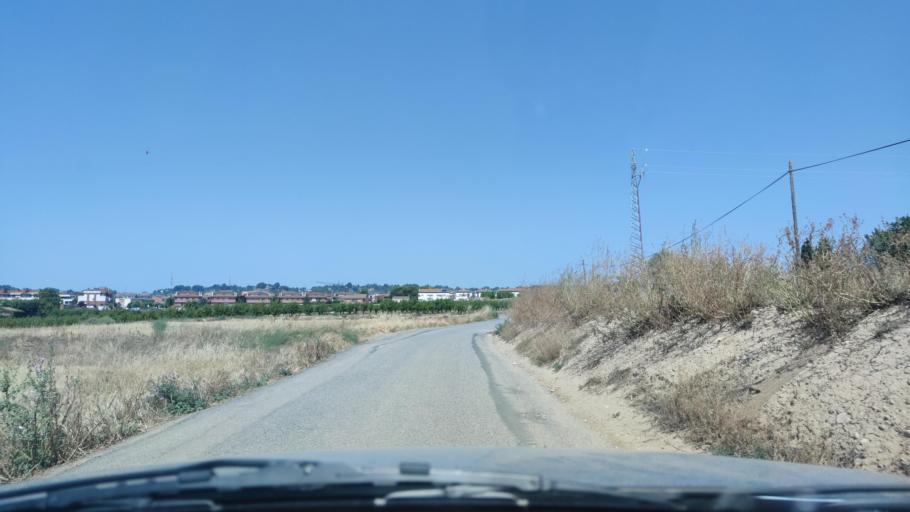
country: ES
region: Catalonia
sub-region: Provincia de Lleida
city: Alpicat
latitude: 41.6596
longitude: 0.5624
